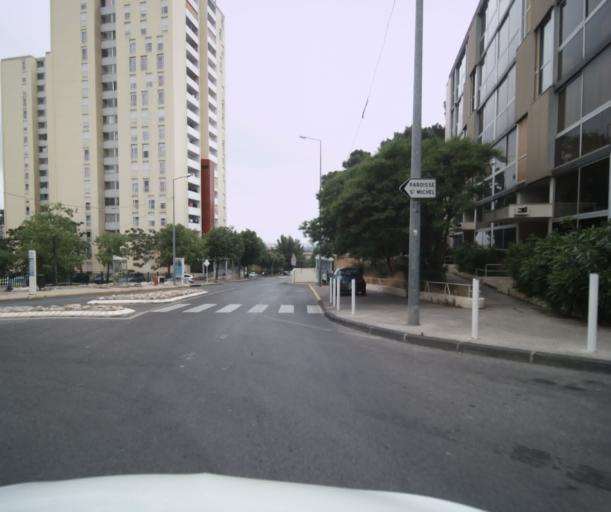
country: FR
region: Provence-Alpes-Cote d'Azur
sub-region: Departement du Var
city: Ollioules
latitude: 43.1322
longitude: 5.8819
